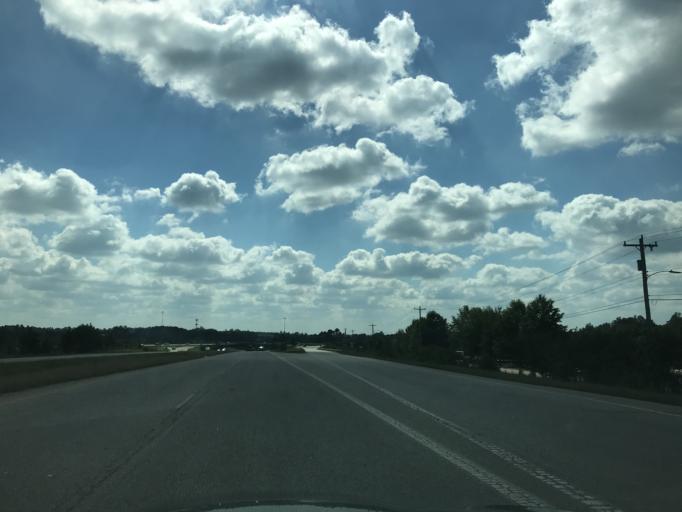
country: US
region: North Carolina
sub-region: Wake County
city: Wake Forest
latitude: 35.9705
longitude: -78.5411
